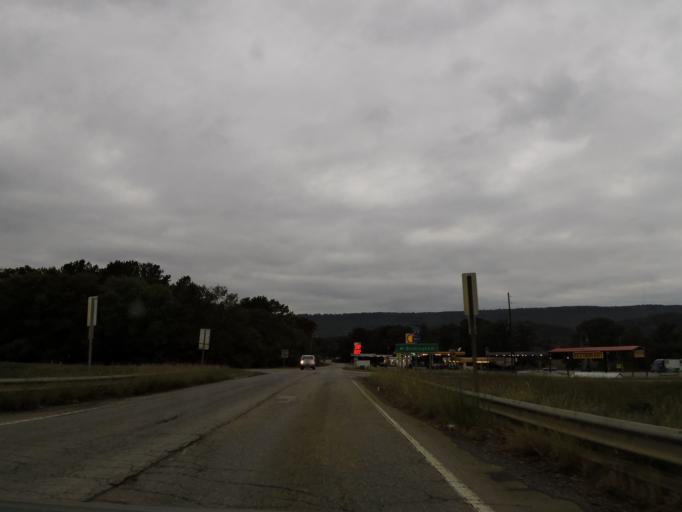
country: US
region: Alabama
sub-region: Saint Clair County
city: Steele
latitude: 33.9337
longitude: -86.1943
